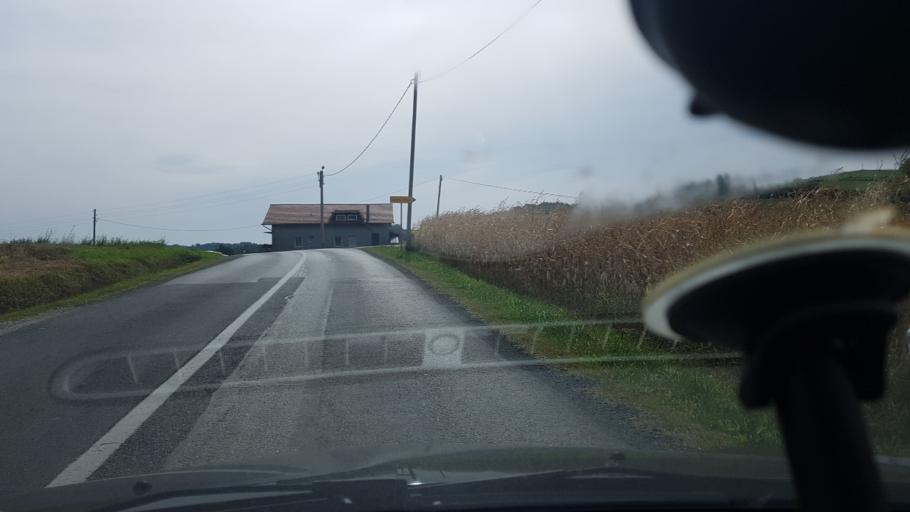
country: HR
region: Varazdinska
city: Ljubescica
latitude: 46.1057
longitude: 16.3645
